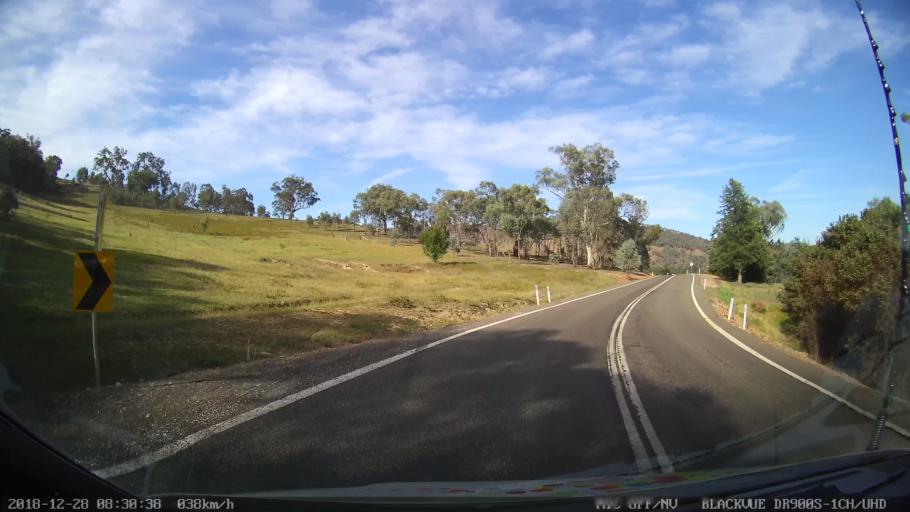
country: AU
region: New South Wales
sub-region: Blayney
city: Blayney
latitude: -33.9569
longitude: 149.3239
